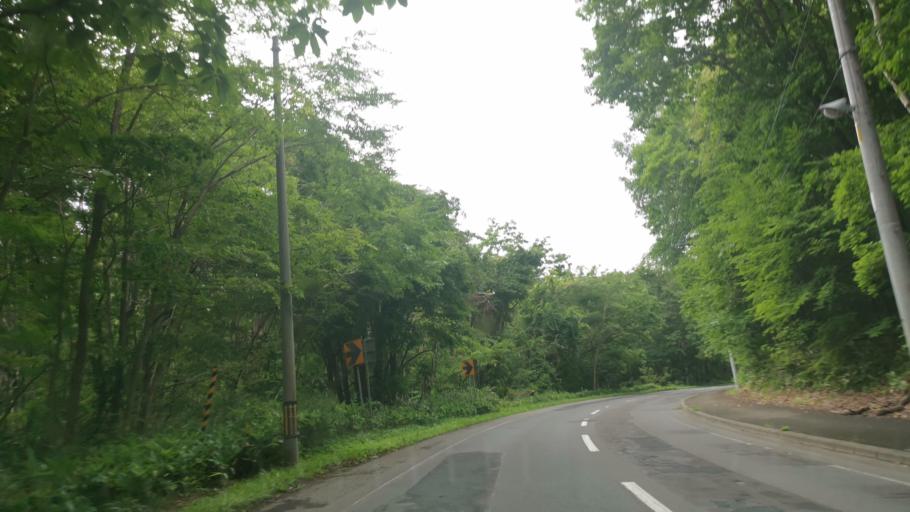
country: JP
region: Hokkaido
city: Sapporo
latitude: 42.9798
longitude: 141.3604
